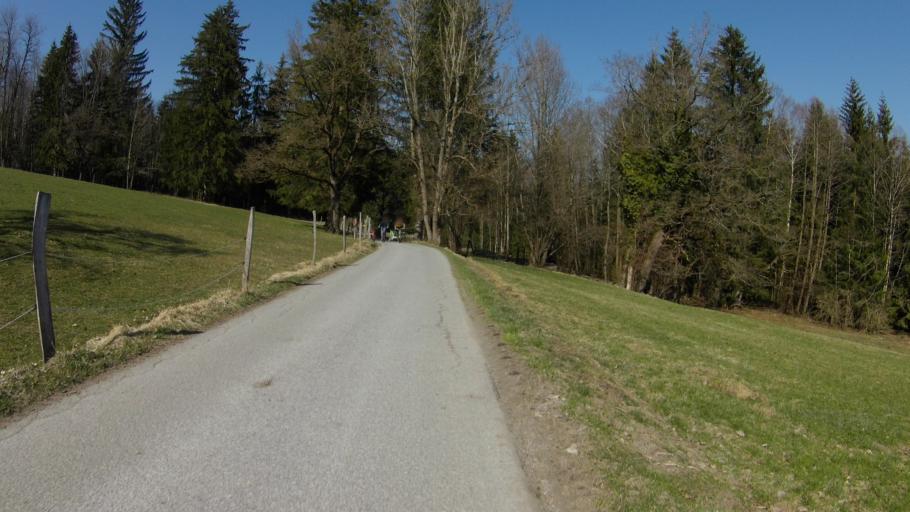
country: DE
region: Bavaria
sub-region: Upper Bavaria
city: Fischbachau
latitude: 47.7272
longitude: 11.9306
